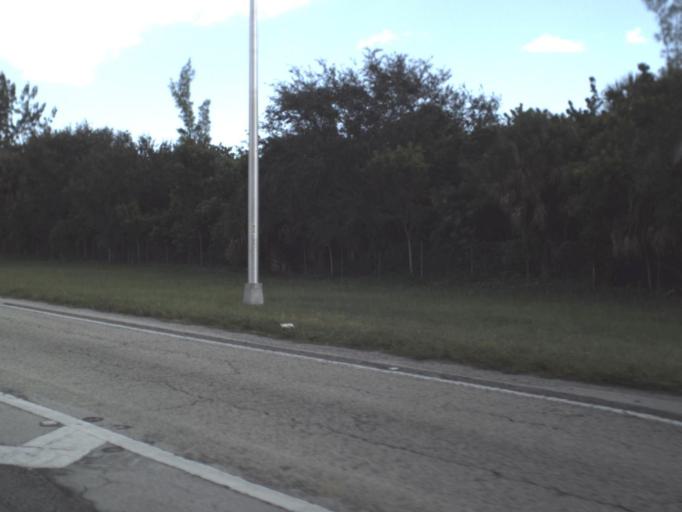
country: US
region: Florida
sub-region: Palm Beach County
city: Plantation Mobile Home Park
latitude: 26.7130
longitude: -80.1377
